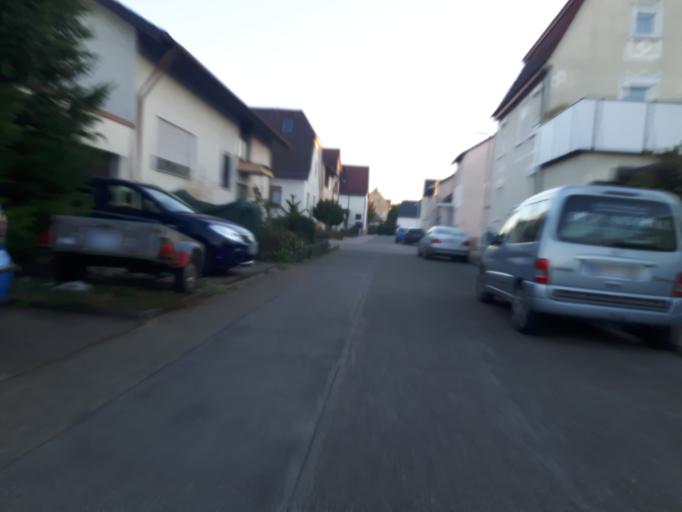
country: DE
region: Baden-Wuerttemberg
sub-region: Regierungsbezirk Stuttgart
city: Untereisesheim
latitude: 49.1982
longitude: 9.2014
